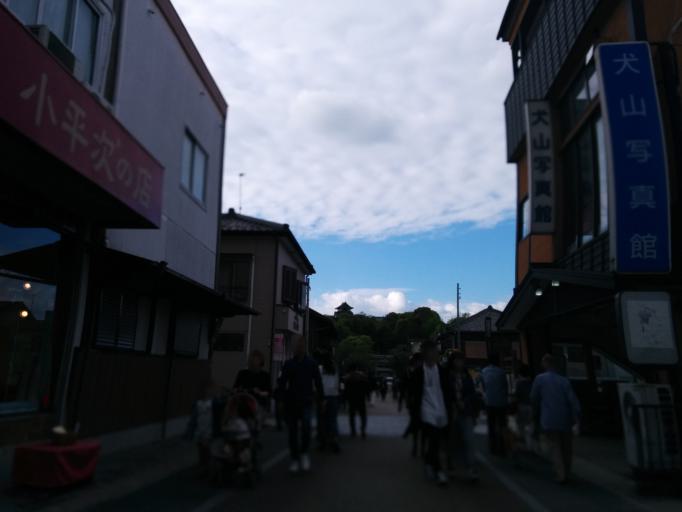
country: JP
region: Gifu
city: Inuyama
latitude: 35.3847
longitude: 136.9395
